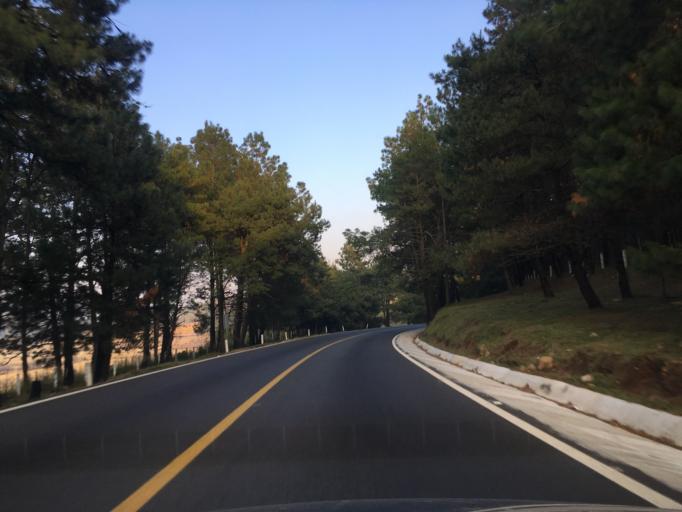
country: MX
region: Michoacan
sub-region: Patzcuaro
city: Santa Maria Huiramangaro (San Juan Tumbio)
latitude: 19.4894
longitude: -101.7867
